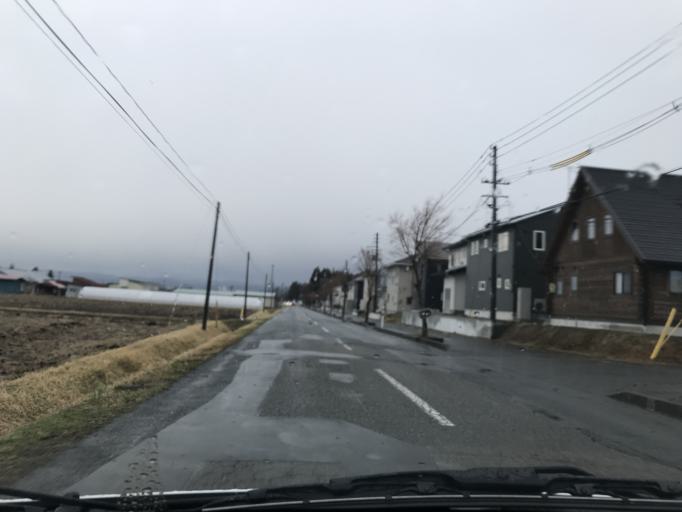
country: JP
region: Iwate
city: Kitakami
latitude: 39.2195
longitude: 141.0783
